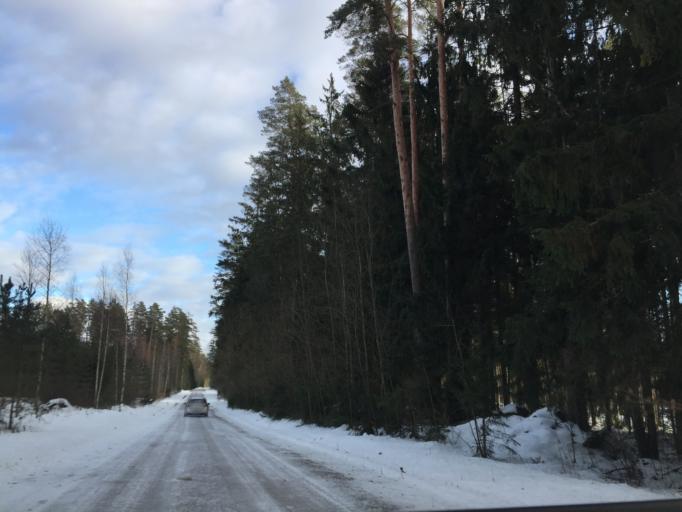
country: LV
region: Lielvarde
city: Lielvarde
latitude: 56.5661
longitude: 24.8176
